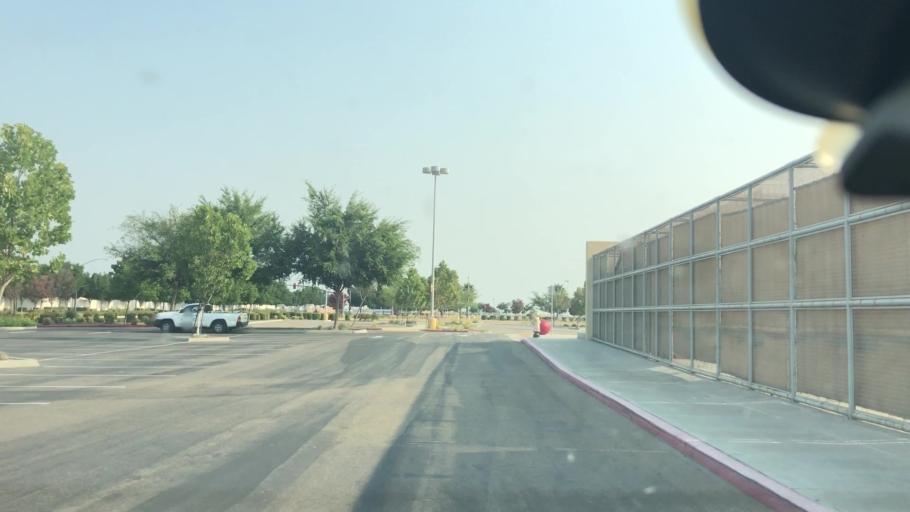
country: US
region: California
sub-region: San Joaquin County
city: Lathrop
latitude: 37.8082
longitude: -121.2995
